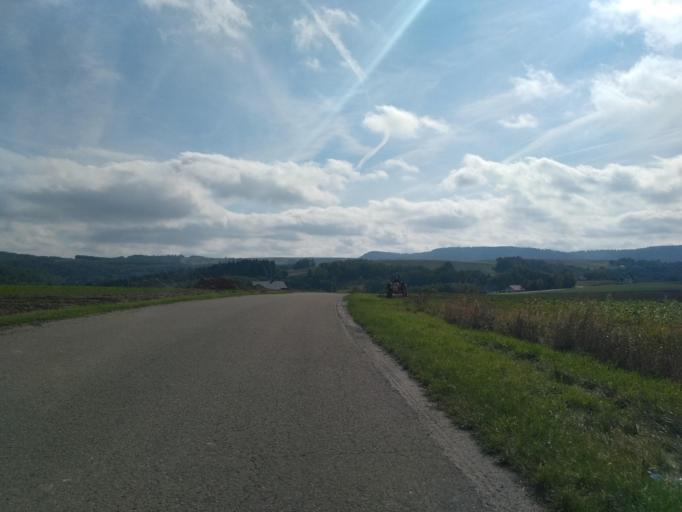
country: PL
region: Subcarpathian Voivodeship
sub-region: Powiat ropczycko-sedziszowski
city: Wielopole Skrzynskie
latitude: 49.9265
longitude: 21.5656
